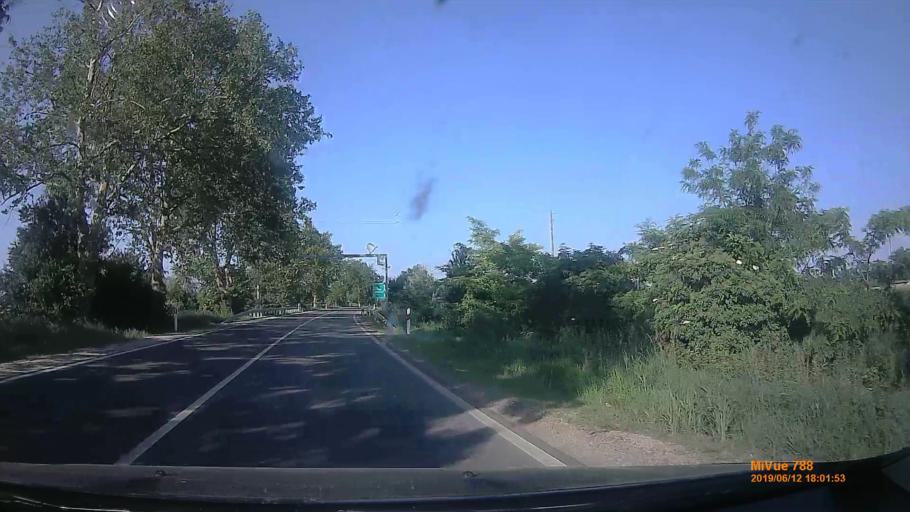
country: HU
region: Csongrad
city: Roszke
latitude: 46.2310
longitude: 20.0809
